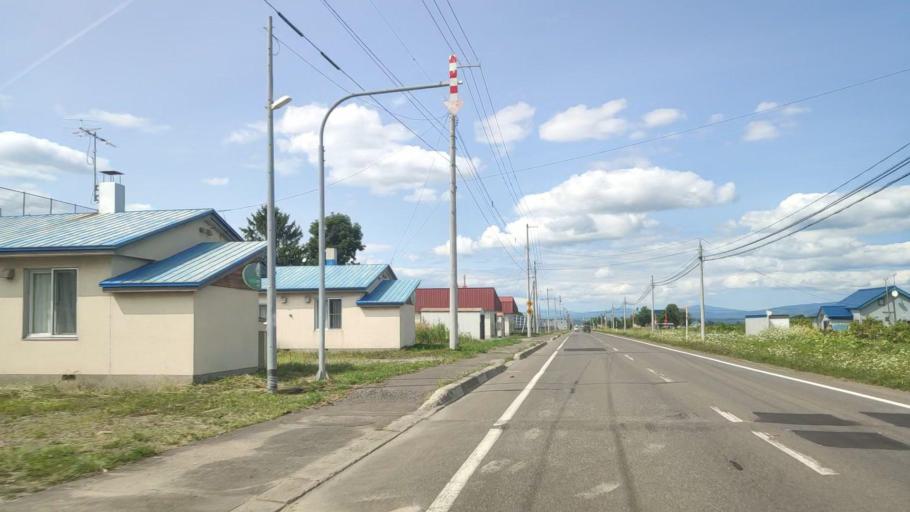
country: JP
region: Hokkaido
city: Nayoro
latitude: 44.2928
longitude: 142.4294
